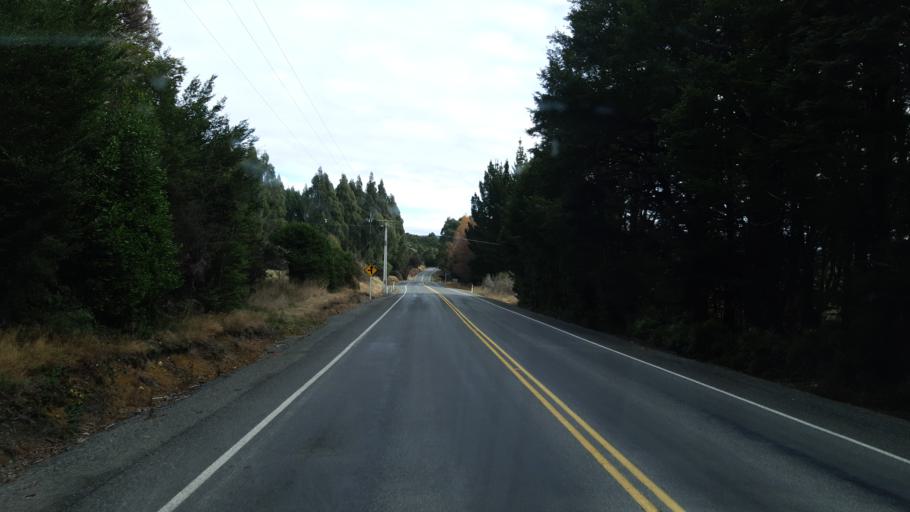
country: NZ
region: Tasman
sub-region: Tasman District
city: Wakefield
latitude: -41.7768
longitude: 172.9218
